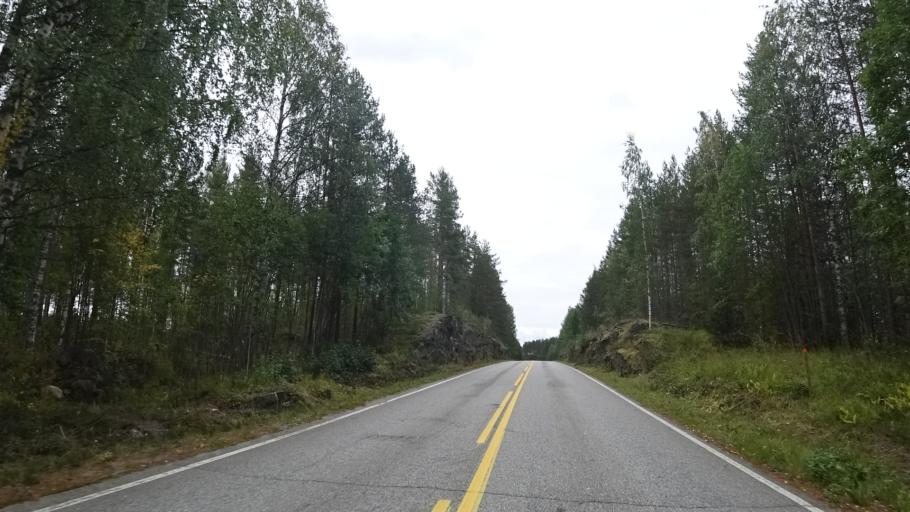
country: FI
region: North Karelia
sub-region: Joensuu
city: Ilomantsi
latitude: 62.6202
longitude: 31.1992
